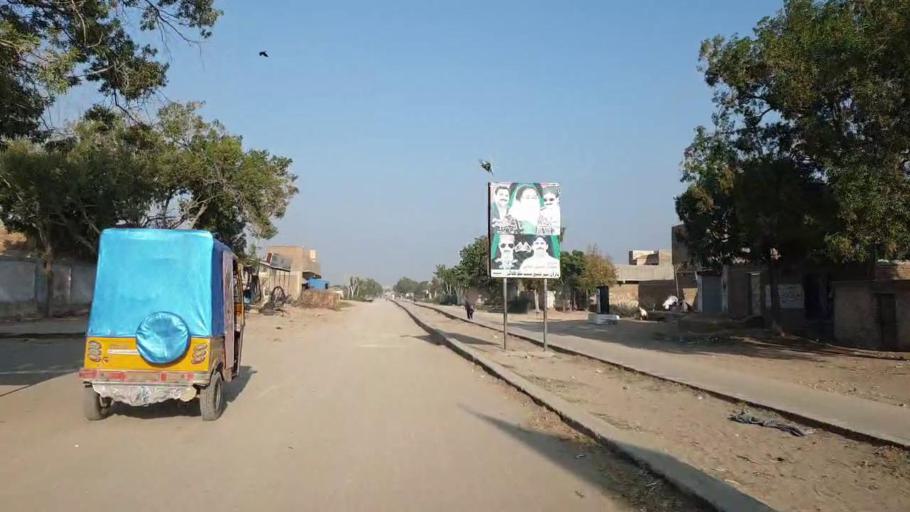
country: PK
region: Sindh
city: Kotri
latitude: 25.3595
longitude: 68.2546
